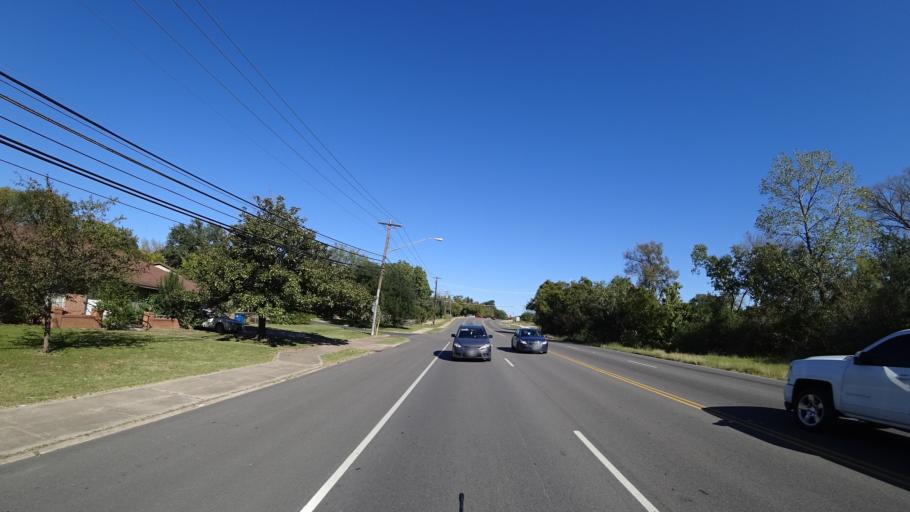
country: US
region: Texas
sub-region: Travis County
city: Austin
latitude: 30.2867
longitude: -97.6743
